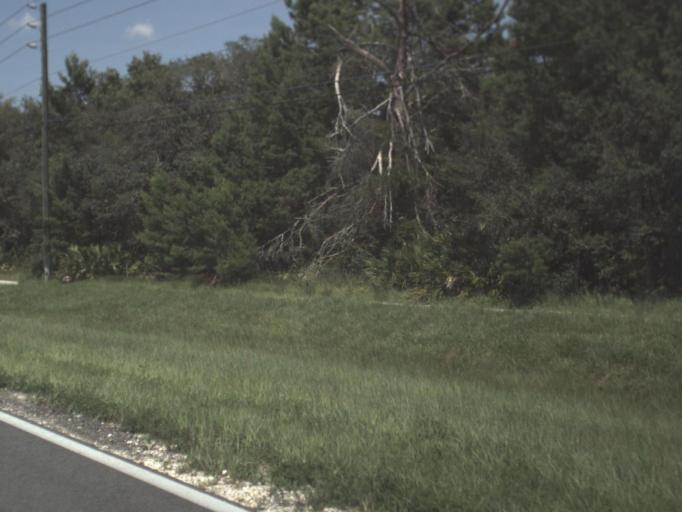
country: US
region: Florida
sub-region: Hernando County
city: North Weeki Wachee
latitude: 28.5708
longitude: -82.5580
